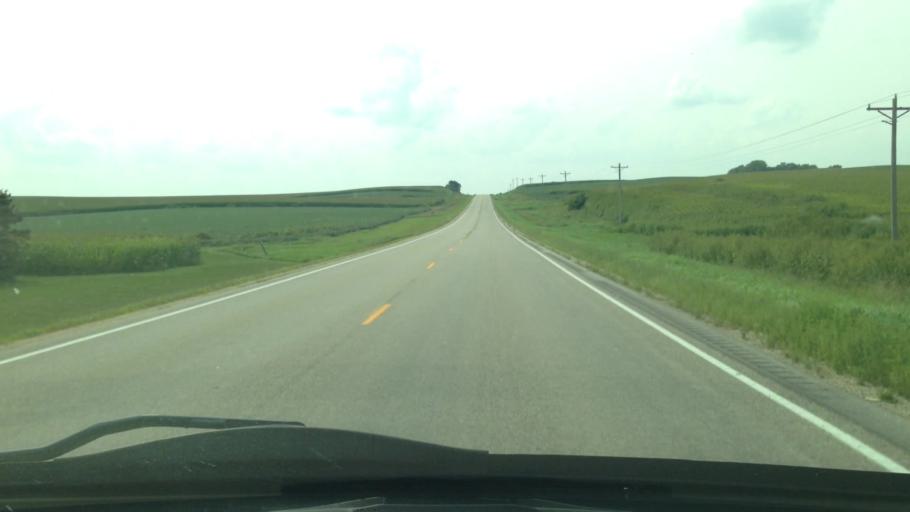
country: US
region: Minnesota
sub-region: Wabasha County
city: Elgin
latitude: 44.1653
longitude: -92.2314
